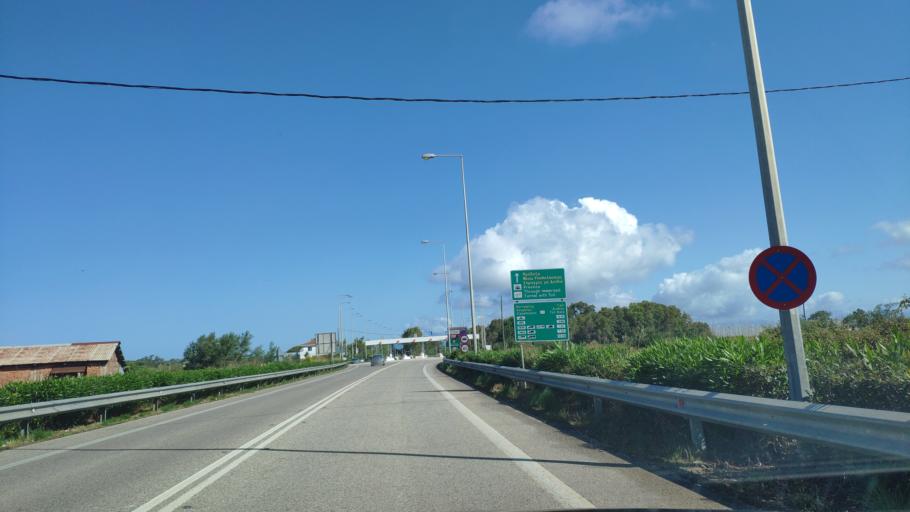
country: GR
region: Epirus
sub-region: Nomos Prevezis
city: Preveza
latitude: 38.9380
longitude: 20.7676
